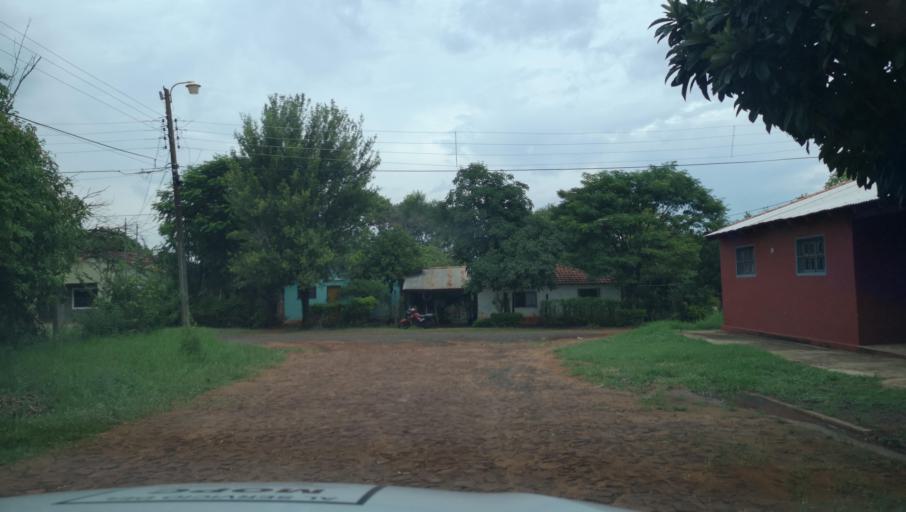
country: PY
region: Misiones
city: Santa Maria
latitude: -26.8896
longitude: -57.0437
